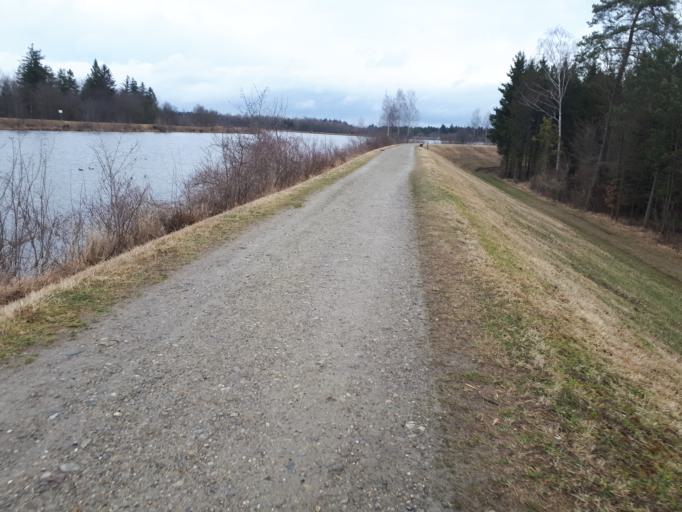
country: DE
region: Bavaria
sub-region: Swabia
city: Bobingen
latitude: 48.2883
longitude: 10.8293
